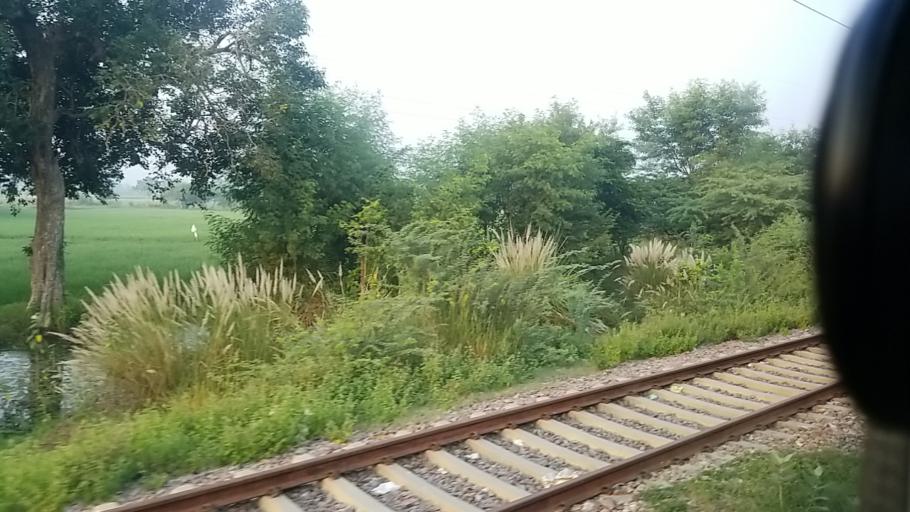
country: IN
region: Uttar Pradesh
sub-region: Kanpur
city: Nawabganj
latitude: 26.4667
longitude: 80.1488
